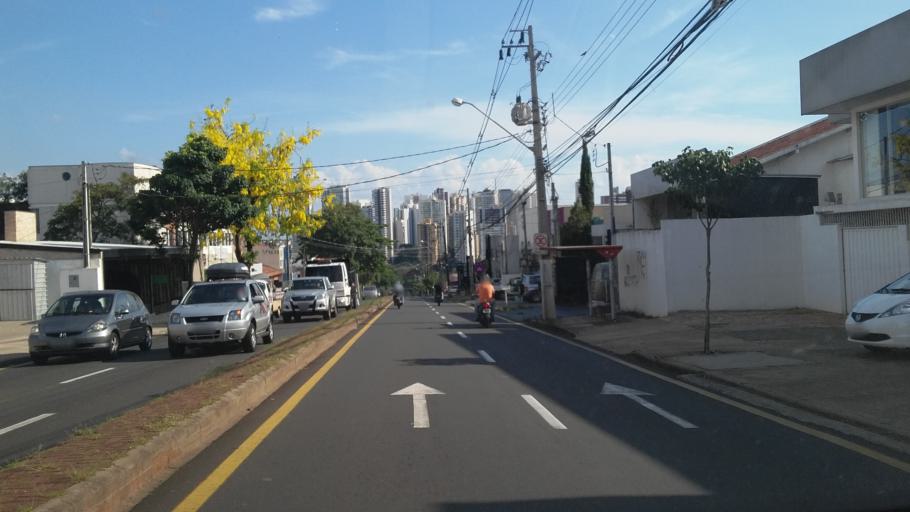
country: BR
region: Parana
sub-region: Londrina
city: Londrina
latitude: -23.3189
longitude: -51.1768
